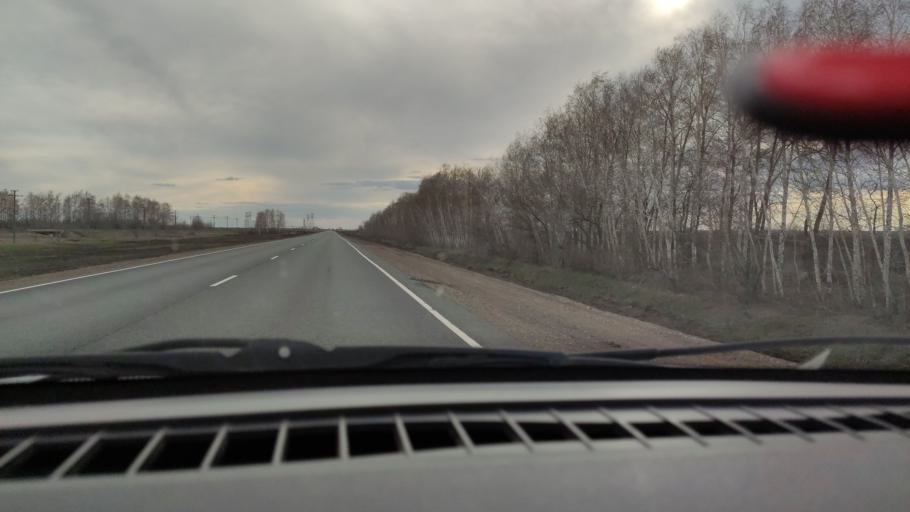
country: RU
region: Bashkortostan
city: Mayachnyy
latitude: 52.3730
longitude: 55.6260
